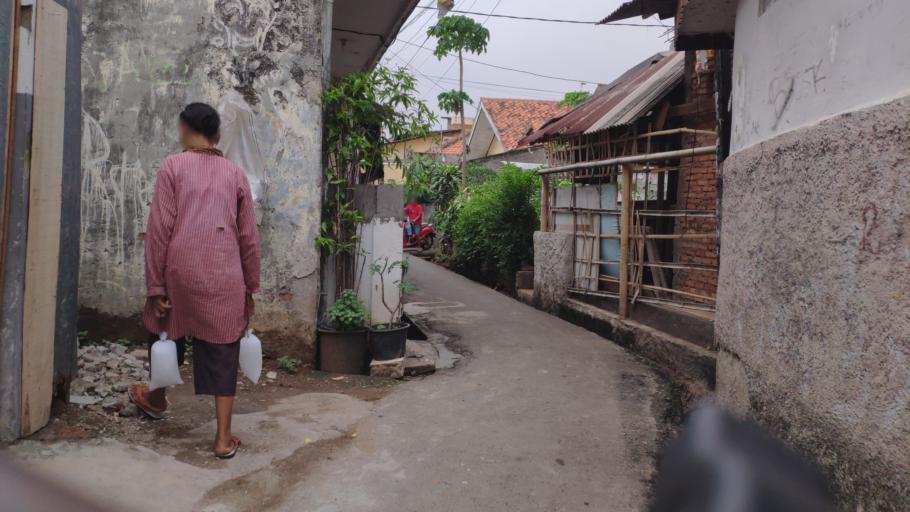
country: ID
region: Jakarta Raya
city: Jakarta
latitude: -6.2156
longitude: 106.8394
